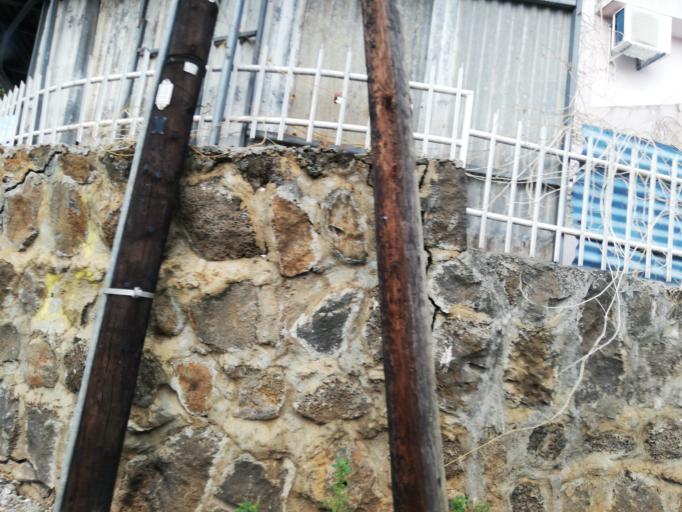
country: MU
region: Black River
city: Petite Riviere
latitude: -20.2016
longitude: 57.4671
